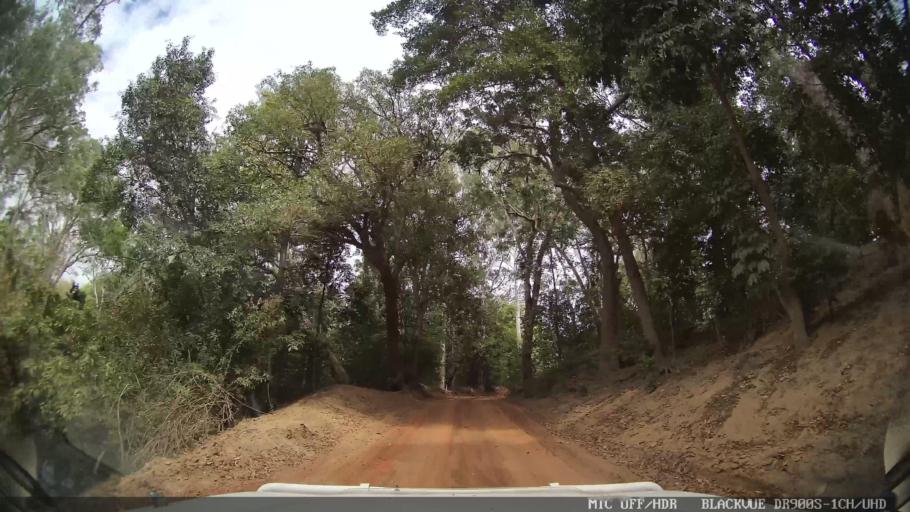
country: AU
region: Queensland
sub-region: Cook
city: Cooktown
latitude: -15.2905
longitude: 144.8446
